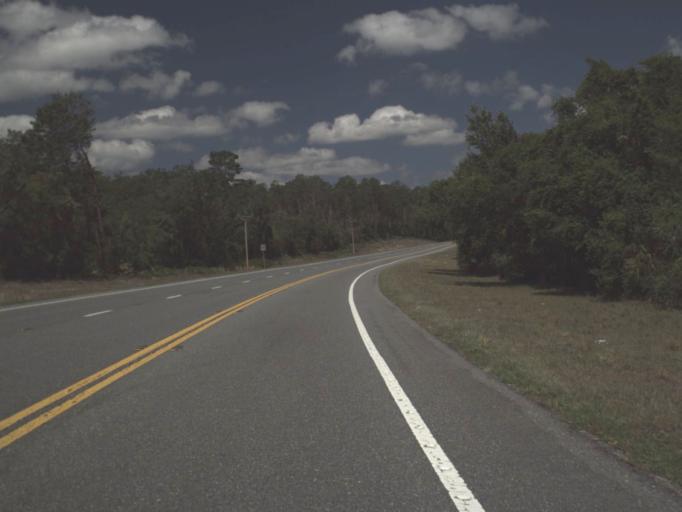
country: US
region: Florida
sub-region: Lake County
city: Astor
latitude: 29.1739
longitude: -81.6905
